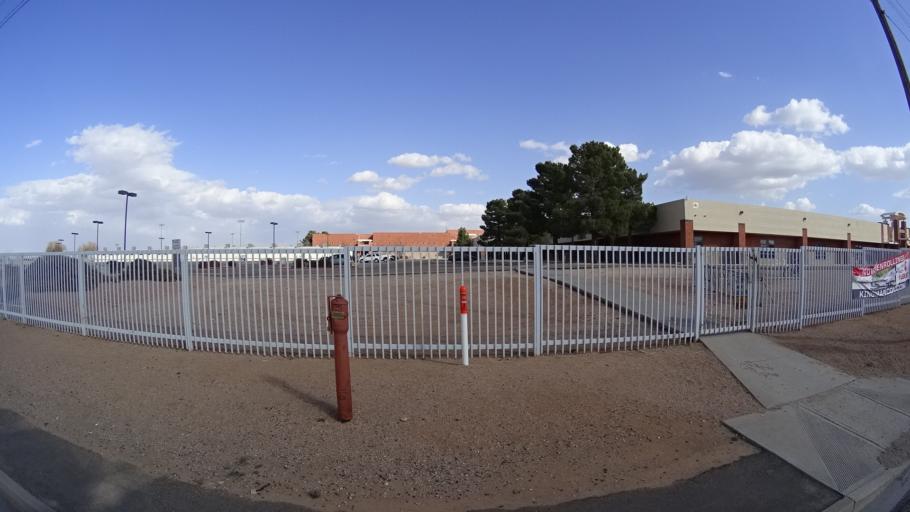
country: US
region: Arizona
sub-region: Mohave County
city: New Kingman-Butler
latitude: 35.2445
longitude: -114.0115
